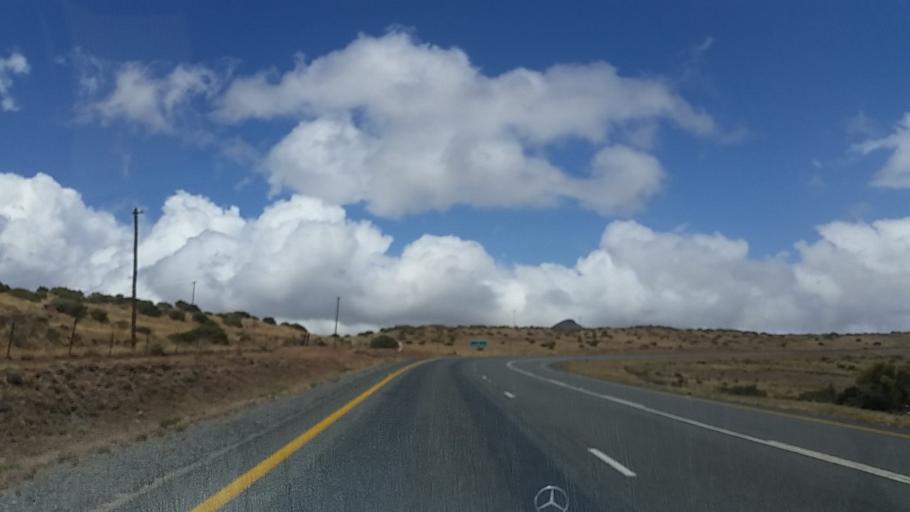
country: ZA
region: Eastern Cape
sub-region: Chris Hani District Municipality
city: Middelburg
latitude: -31.7909
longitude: 24.8975
